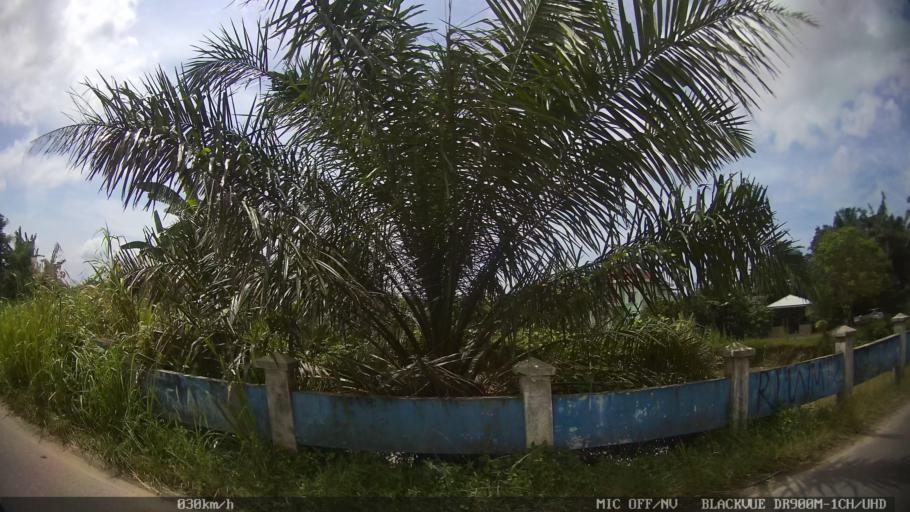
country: ID
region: North Sumatra
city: Percut
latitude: 3.6077
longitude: 98.8421
